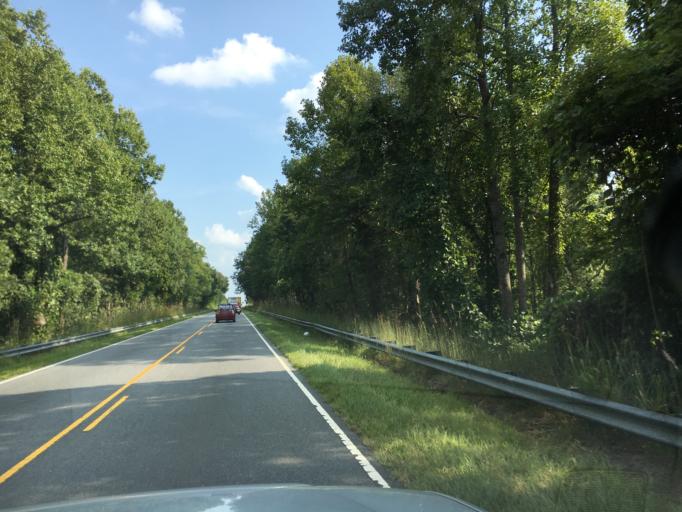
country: US
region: North Carolina
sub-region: Rutherford County
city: Rutherfordton
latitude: 35.4124
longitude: -81.9720
